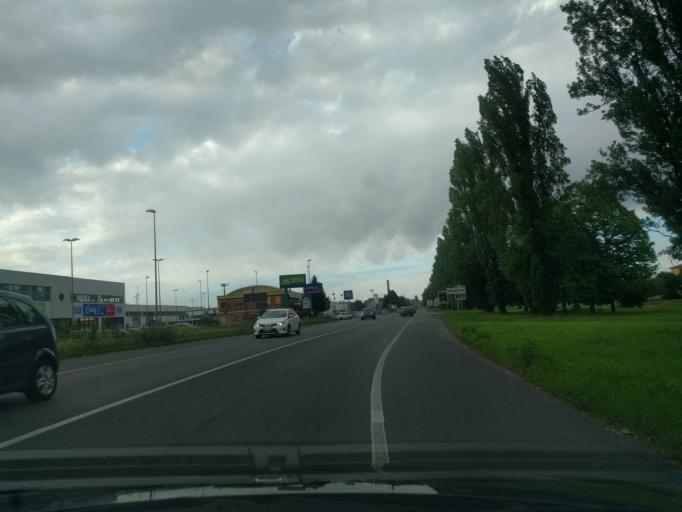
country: IT
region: Veneto
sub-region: Provincia di Rovigo
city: Santa Maria Maddalena
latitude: 44.8729
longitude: 11.6021
